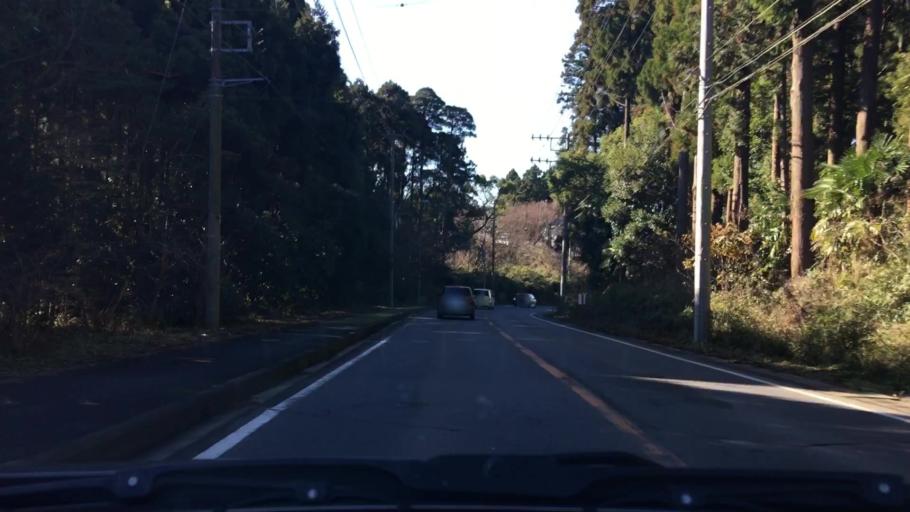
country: JP
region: Chiba
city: Sawara
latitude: 35.8380
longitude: 140.5428
